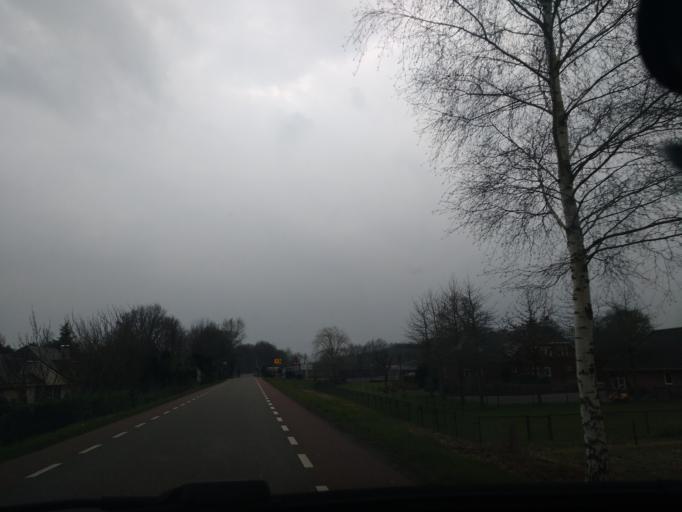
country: NL
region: Utrecht
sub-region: Gemeente Utrechtse Heuvelrug
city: Overberg
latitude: 52.0328
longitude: 5.5233
